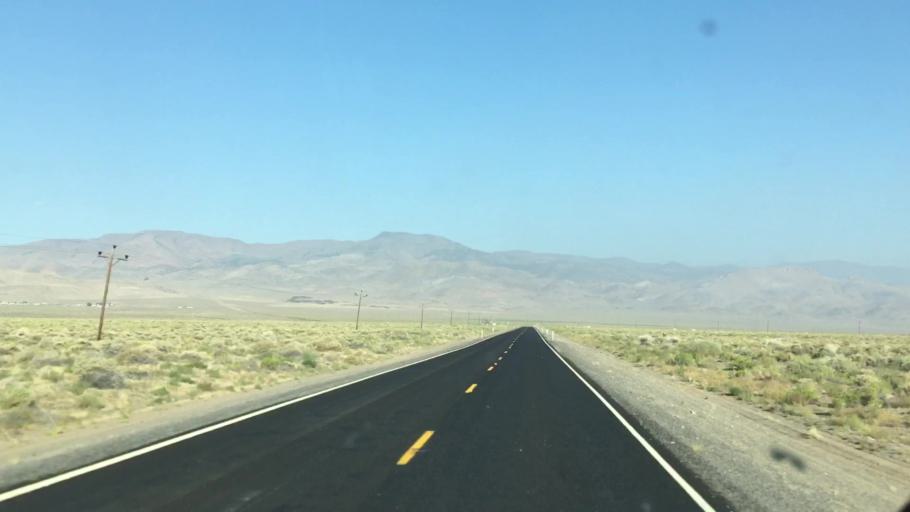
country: US
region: Nevada
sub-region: Lyon County
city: Fernley
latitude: 39.6469
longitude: -119.3146
